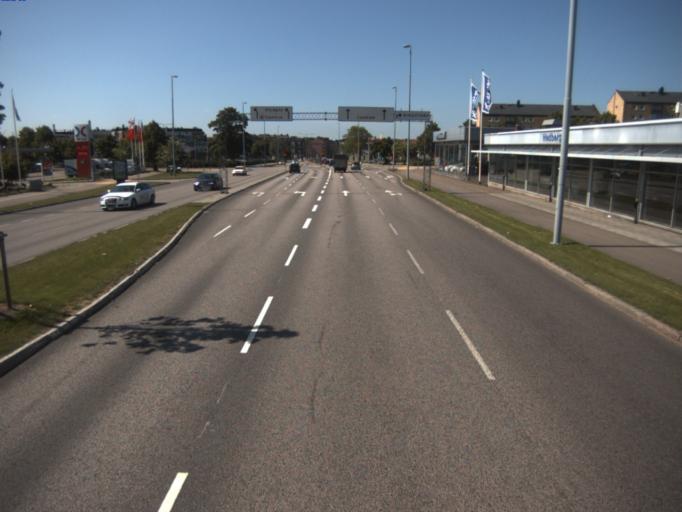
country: SE
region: Skane
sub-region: Helsingborg
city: Helsingborg
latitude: 56.0593
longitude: 12.7050
